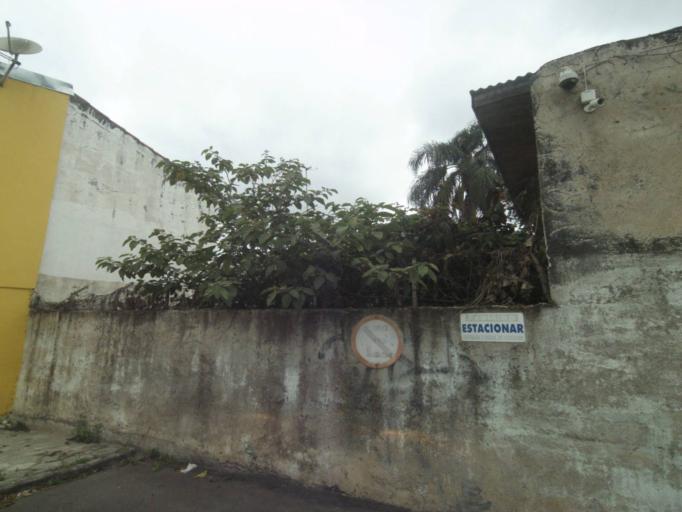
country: BR
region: Parana
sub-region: Sao Jose Dos Pinhais
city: Sao Jose dos Pinhais
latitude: -25.5410
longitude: -49.2752
